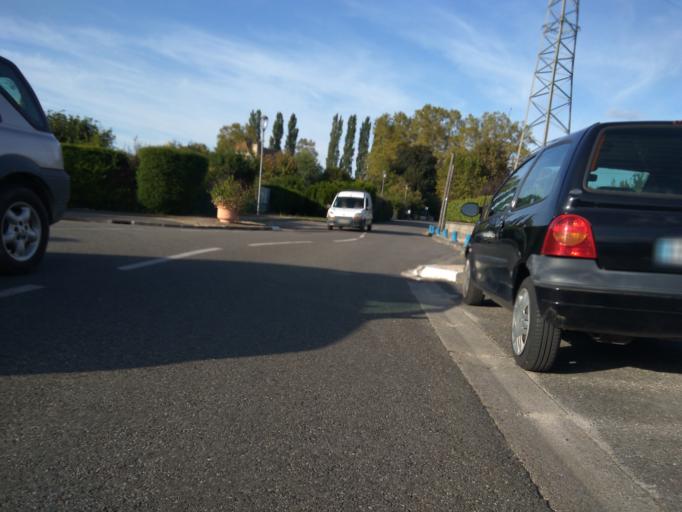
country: FR
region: Aquitaine
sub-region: Departement des Pyrenees-Atlantiques
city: Bizanos
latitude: 43.2813
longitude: -0.3543
